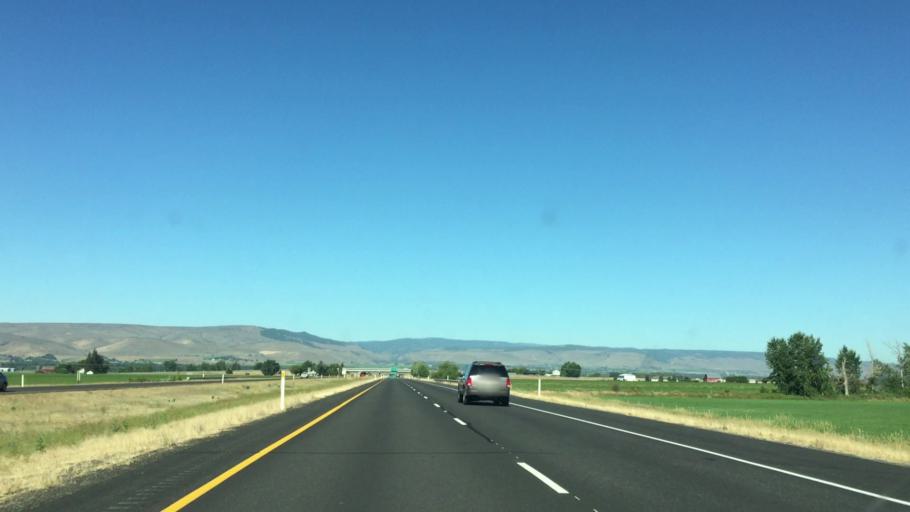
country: US
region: Washington
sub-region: Kittitas County
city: Ellensburg
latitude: 46.9711
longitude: -120.4855
